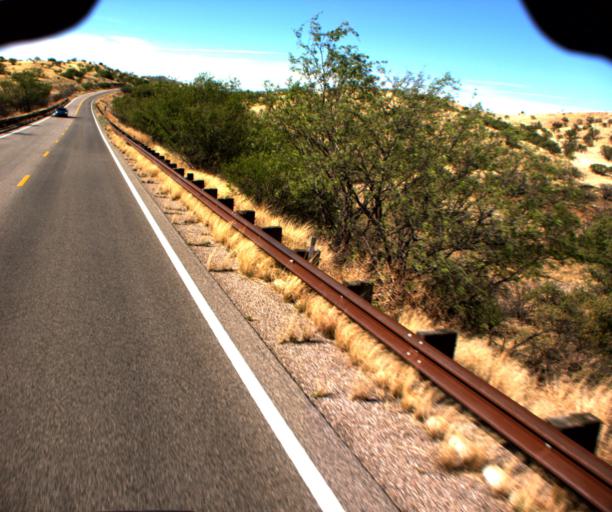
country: US
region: Arizona
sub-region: Pima County
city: Corona de Tucson
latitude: 31.8083
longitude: -110.7095
